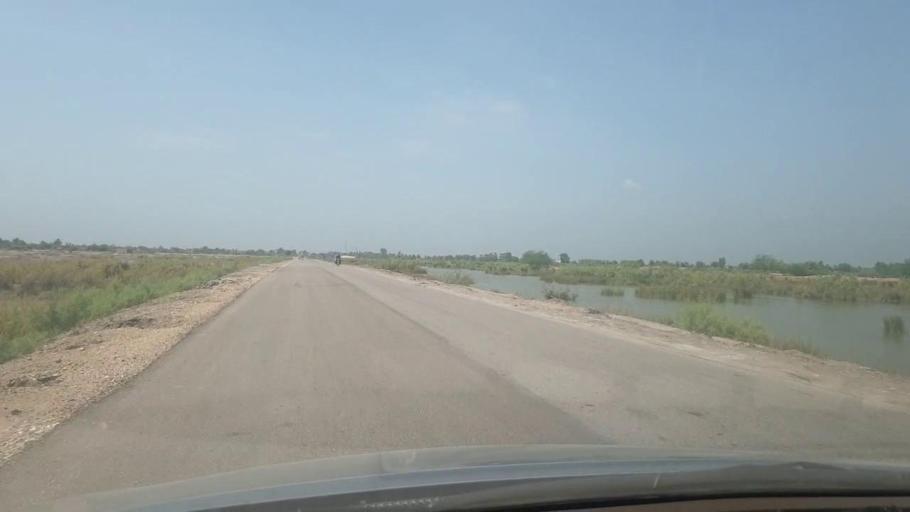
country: PK
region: Sindh
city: Bozdar
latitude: 27.2353
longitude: 68.5707
